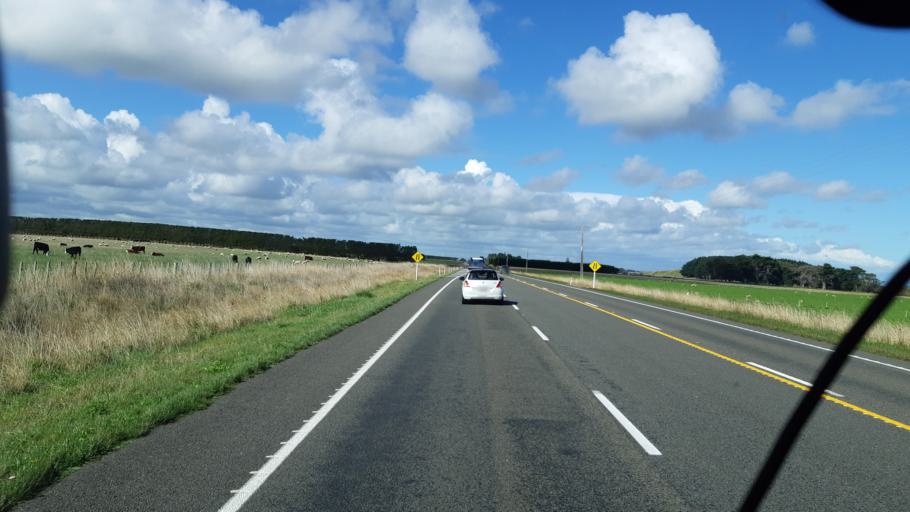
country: NZ
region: Manawatu-Wanganui
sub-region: Wanganui District
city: Wanganui
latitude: -39.9854
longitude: 175.1551
